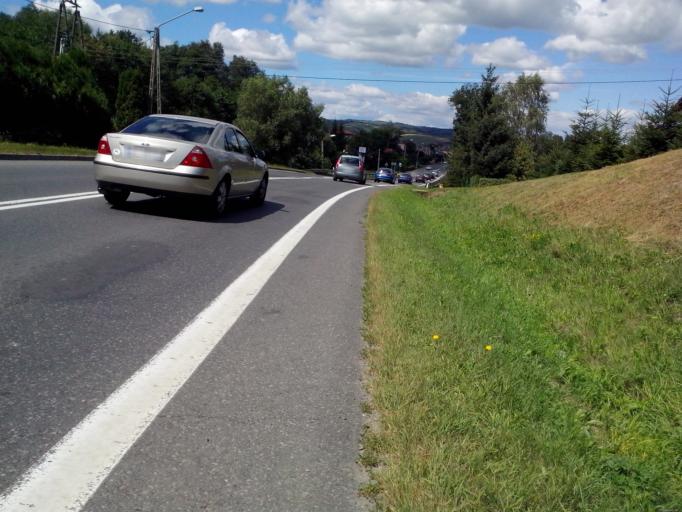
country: PL
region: Subcarpathian Voivodeship
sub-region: Powiat brzozowski
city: Domaradz
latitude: 49.7841
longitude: 21.9485
